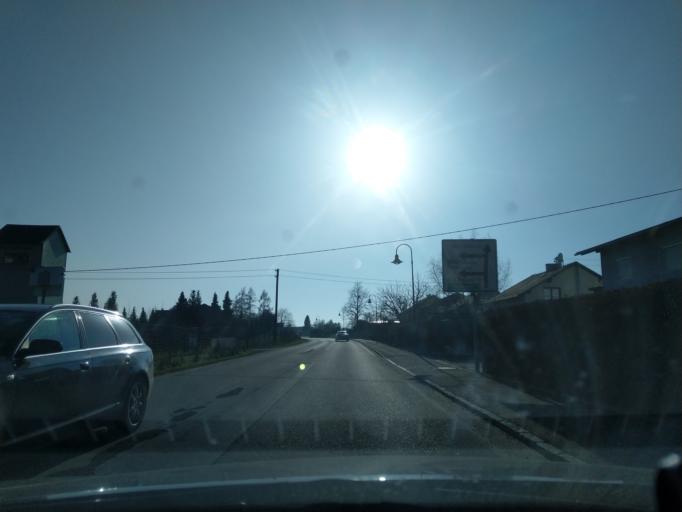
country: DE
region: Bavaria
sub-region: Lower Bavaria
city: Bad Fussing
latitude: 48.3162
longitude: 13.3263
